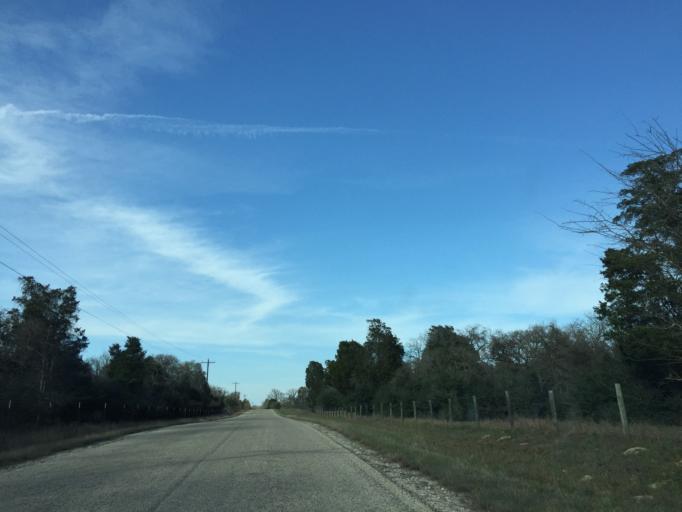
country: US
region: Texas
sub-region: Milam County
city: Thorndale
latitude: 30.4510
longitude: -97.1939
